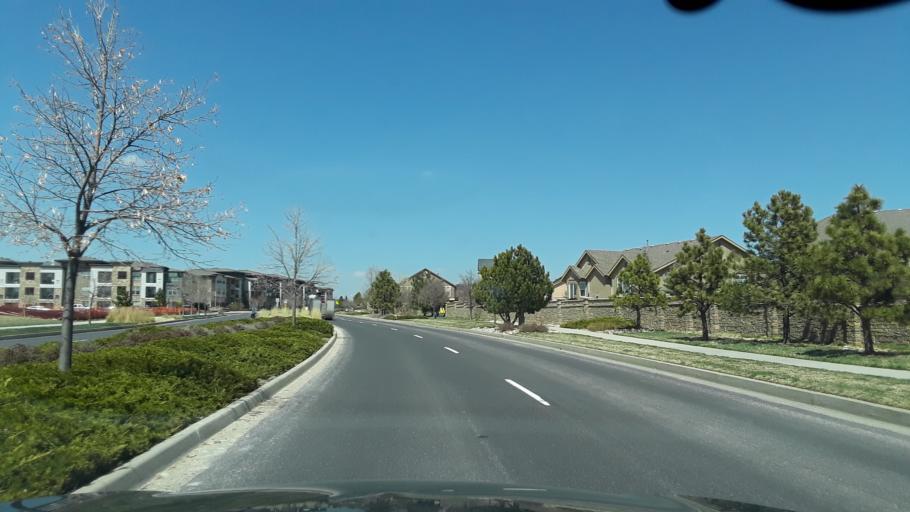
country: US
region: Colorado
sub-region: El Paso County
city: Black Forest
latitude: 38.9728
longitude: -104.7389
